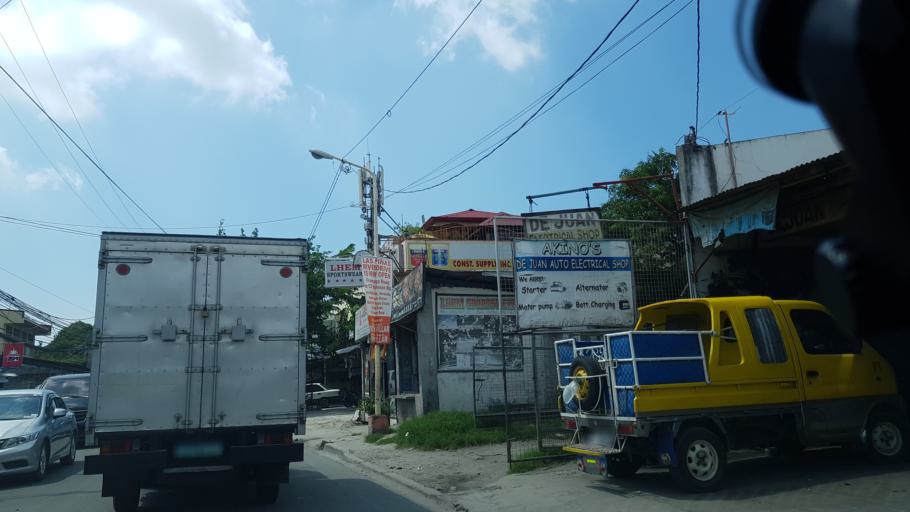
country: PH
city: Sambayanihan People's Village
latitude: 14.4613
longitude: 120.9933
